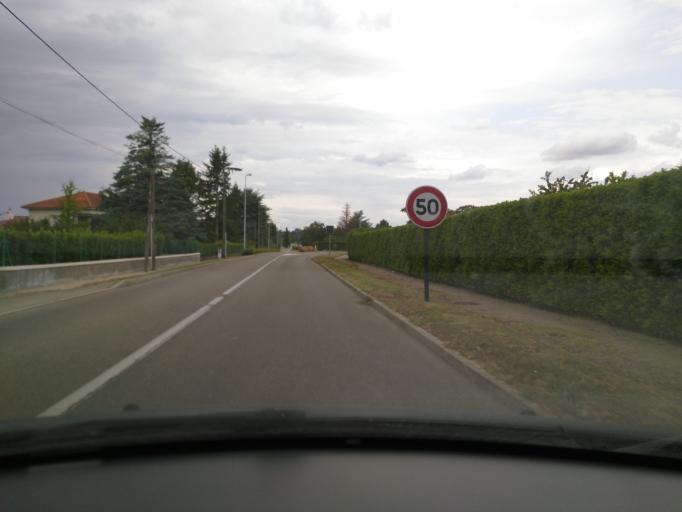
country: FR
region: Rhone-Alpes
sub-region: Departement de l'Isere
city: Beaurepaire
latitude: 45.3511
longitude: 5.0371
